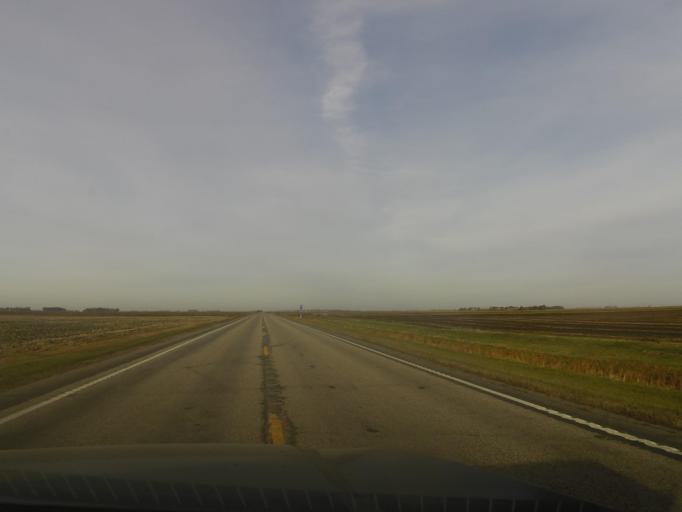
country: US
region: North Dakota
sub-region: Pembina County
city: Cavalier
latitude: 48.8038
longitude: -97.3777
